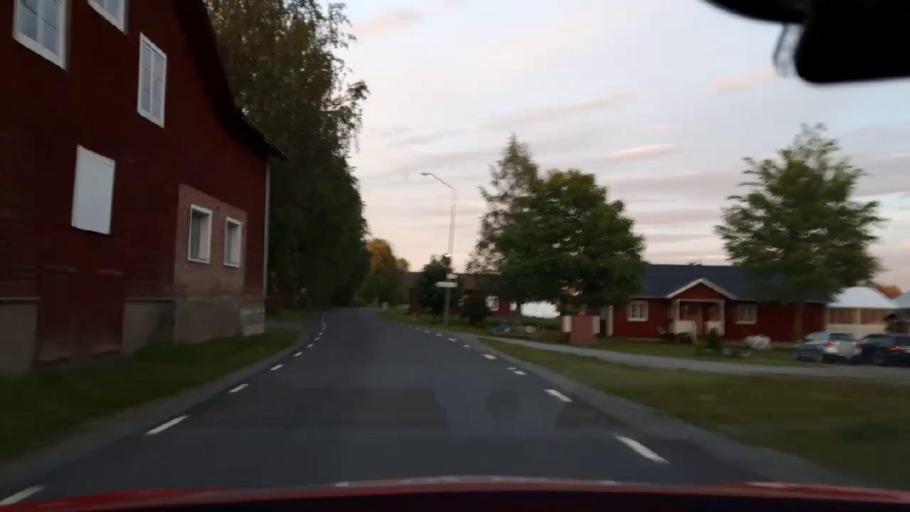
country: SE
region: Jaemtland
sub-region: OEstersunds Kommun
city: Brunflo
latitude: 63.0567
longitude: 14.8128
